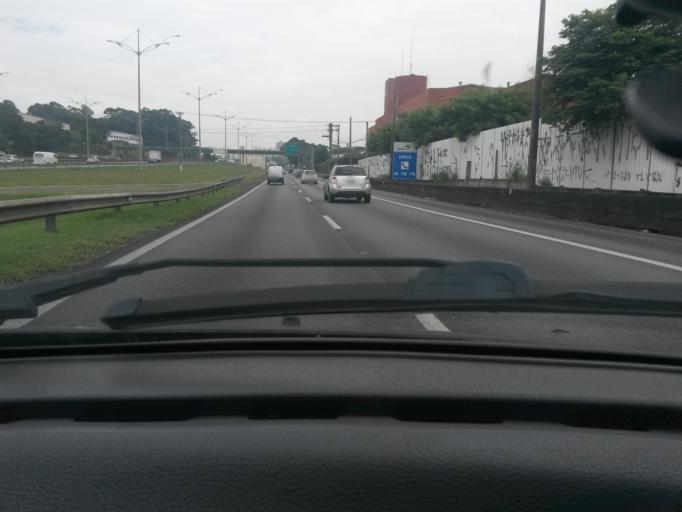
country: BR
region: Sao Paulo
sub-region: Sao Caetano Do Sul
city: Sao Caetano do Sul
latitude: -23.6433
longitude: -46.5856
